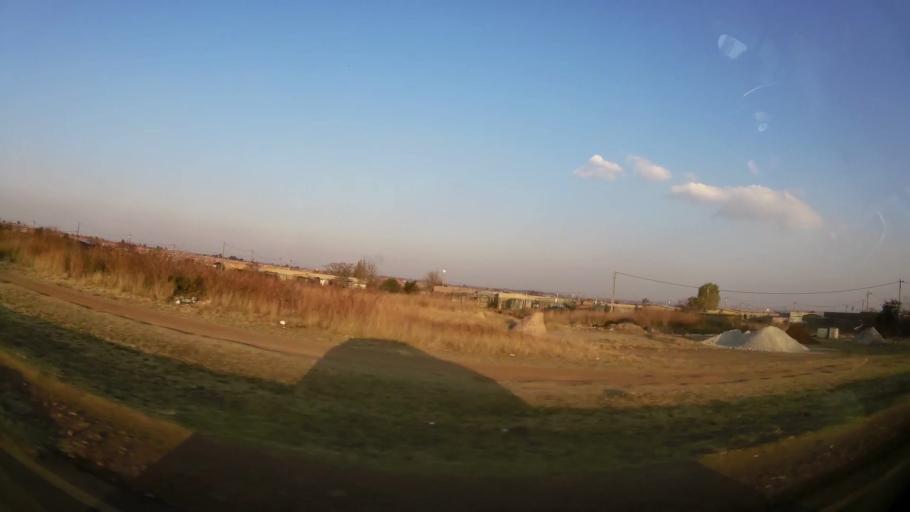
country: ZA
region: Gauteng
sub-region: Ekurhuleni Metropolitan Municipality
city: Benoni
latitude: -26.1520
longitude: 28.3807
